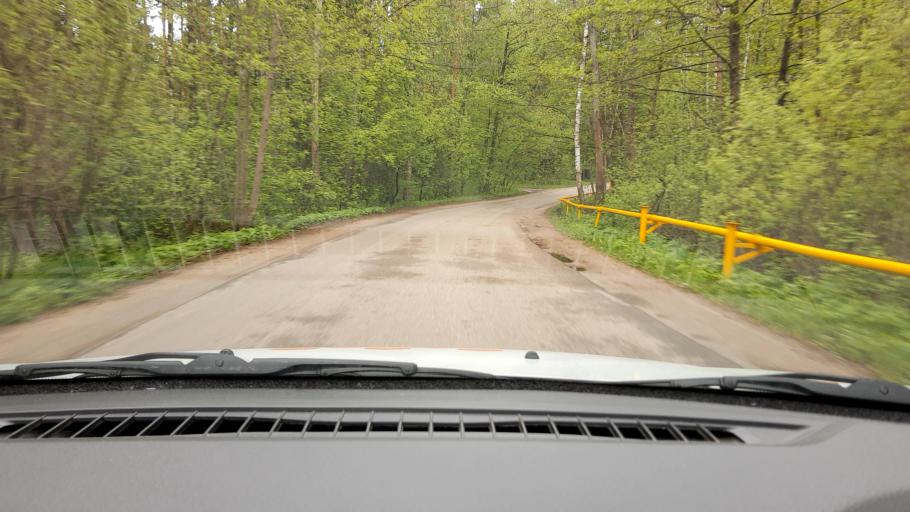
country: RU
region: Nizjnij Novgorod
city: Afonino
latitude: 56.1811
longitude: 44.0799
